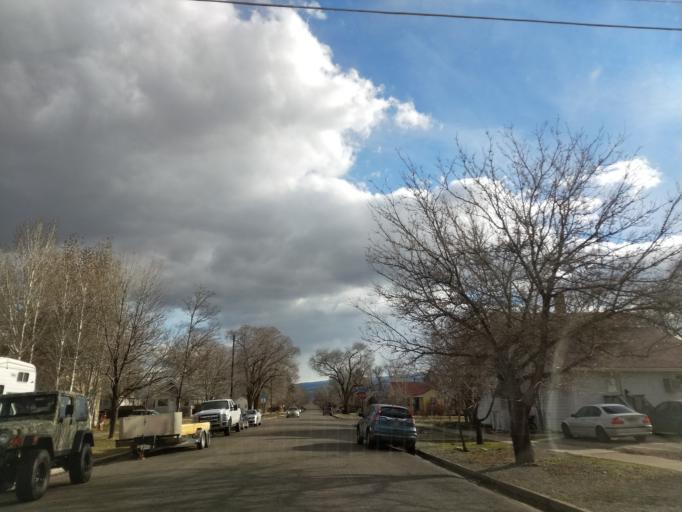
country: US
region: Colorado
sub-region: Mesa County
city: Grand Junction
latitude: 39.0741
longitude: -108.5696
